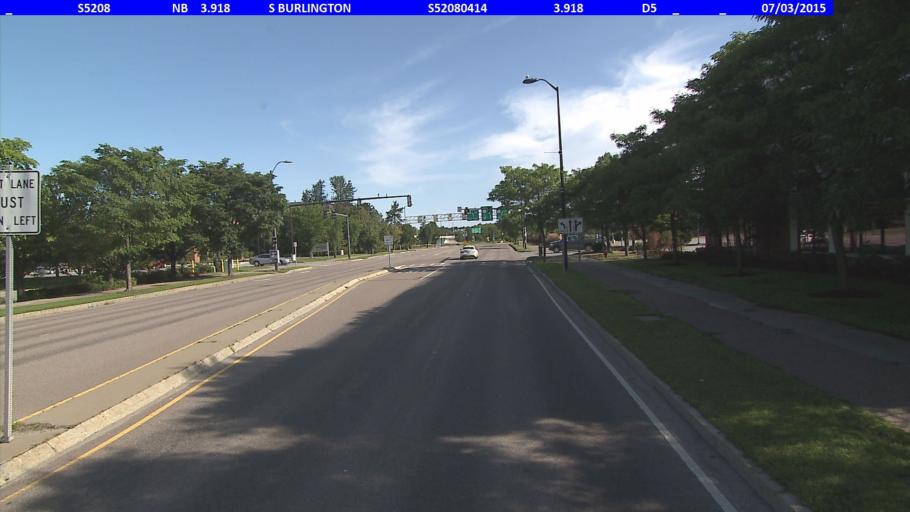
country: US
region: Vermont
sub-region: Chittenden County
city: South Burlington
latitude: 44.4665
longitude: -73.1812
